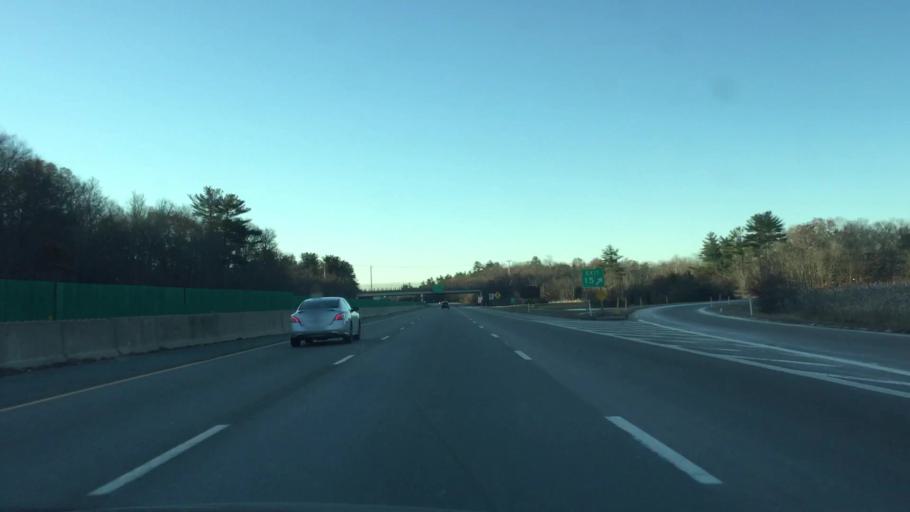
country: US
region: Massachusetts
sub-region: Bristol County
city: Raynham
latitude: 41.9693
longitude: -71.0274
